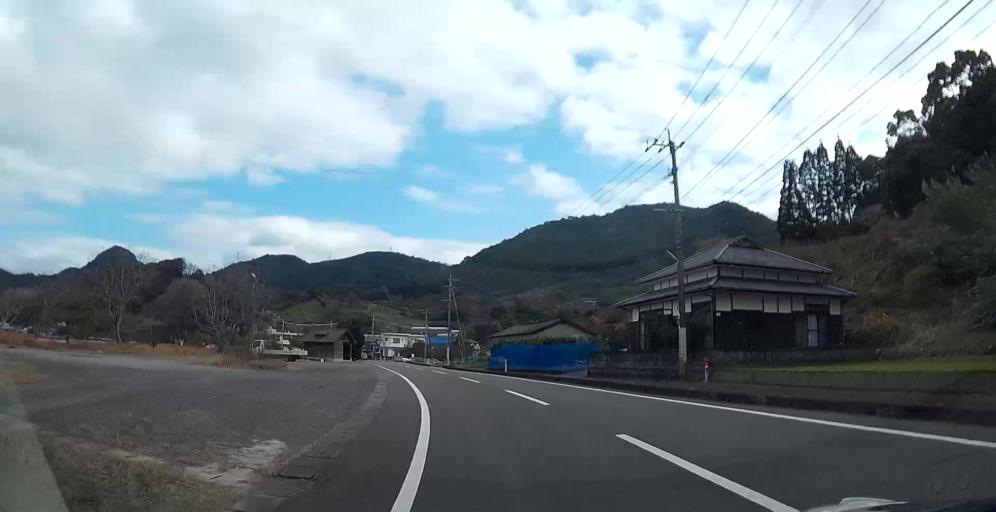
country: JP
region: Kumamoto
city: Minamata
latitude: 32.3269
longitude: 130.4793
